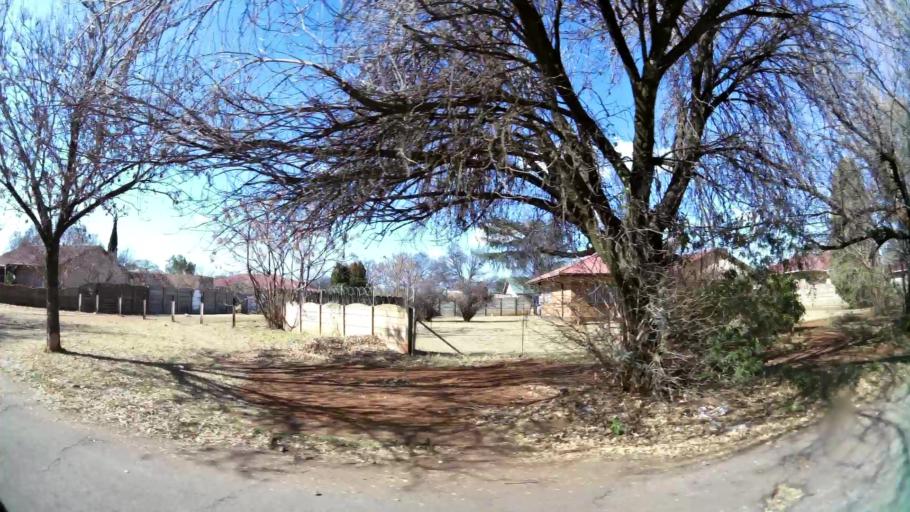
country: ZA
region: Gauteng
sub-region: West Rand District Municipality
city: Carletonville
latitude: -26.3542
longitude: 27.3893
